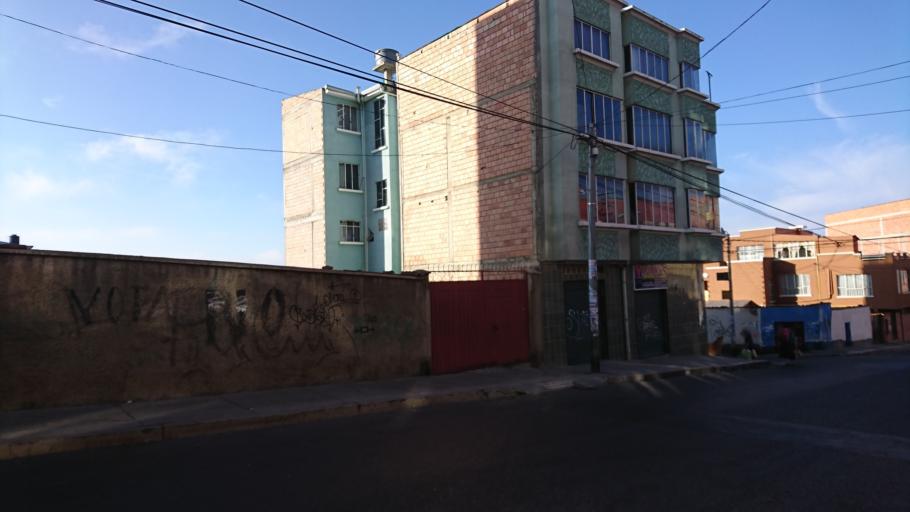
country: BO
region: La Paz
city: La Paz
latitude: -16.4980
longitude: -68.1044
